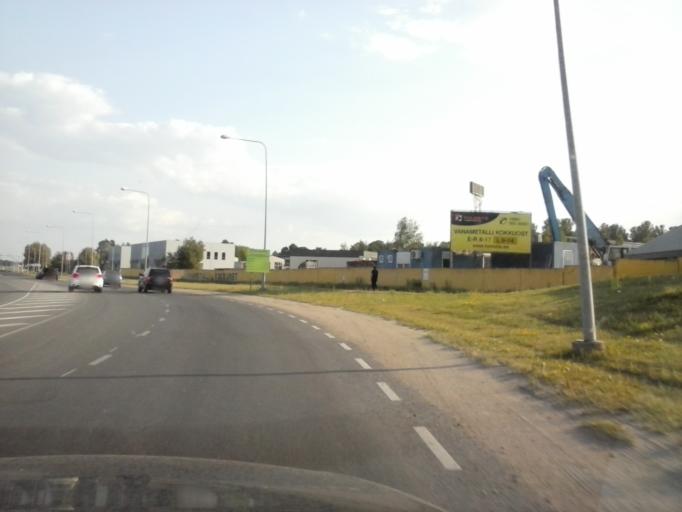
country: EE
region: Tartu
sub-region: Tartu linn
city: Tartu
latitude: 58.3580
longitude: 26.7406
